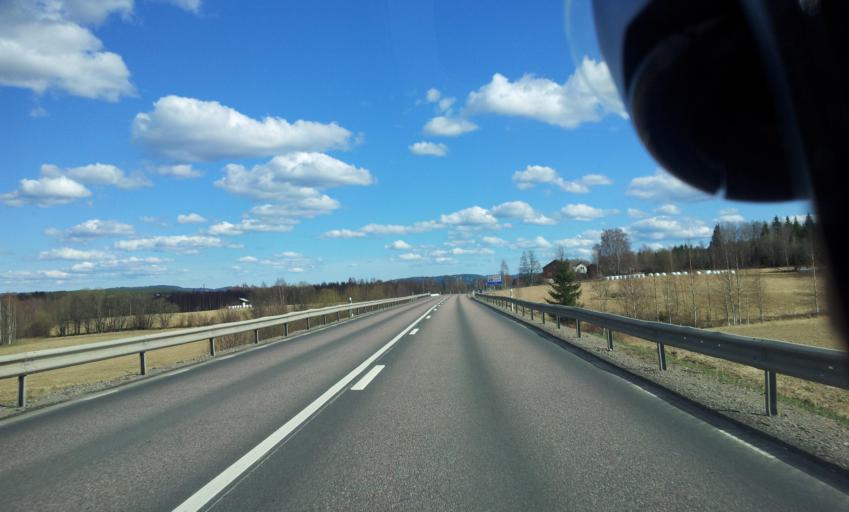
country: SE
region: Gaevleborg
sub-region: Ljusdals Kommun
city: Ljusdal
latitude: 61.8247
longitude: 16.0436
